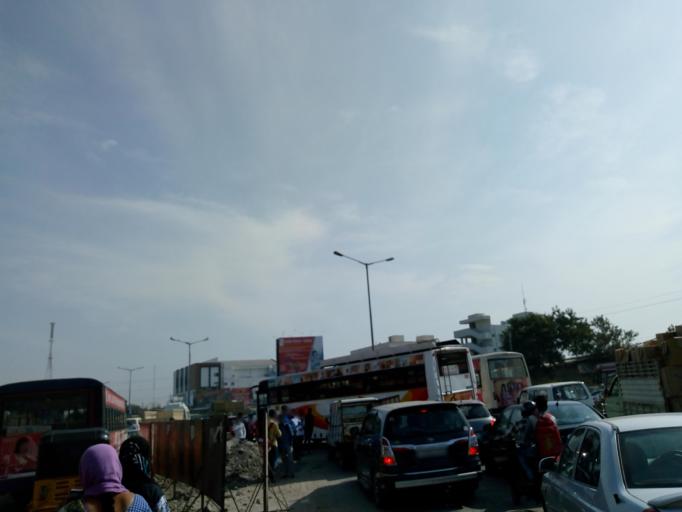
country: IN
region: Telangana
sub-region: Rangareddi
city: Lal Bahadur Nagar
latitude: 17.3455
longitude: 78.5528
